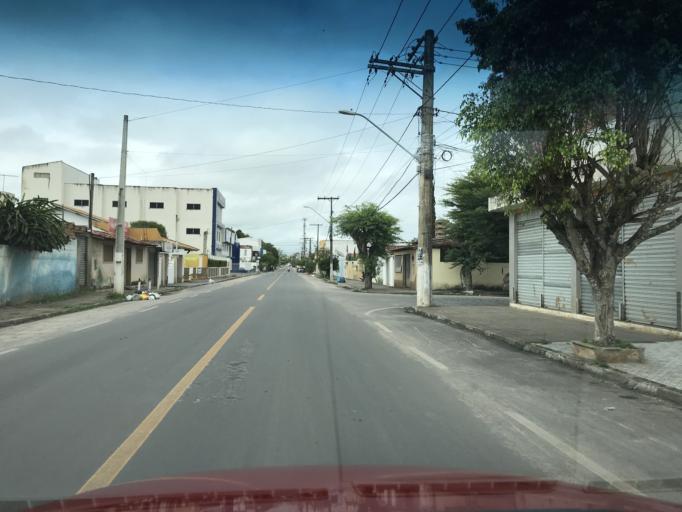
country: BR
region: Bahia
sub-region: Cruz Das Almas
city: Cruz das Almas
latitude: -12.6676
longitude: -39.1005
